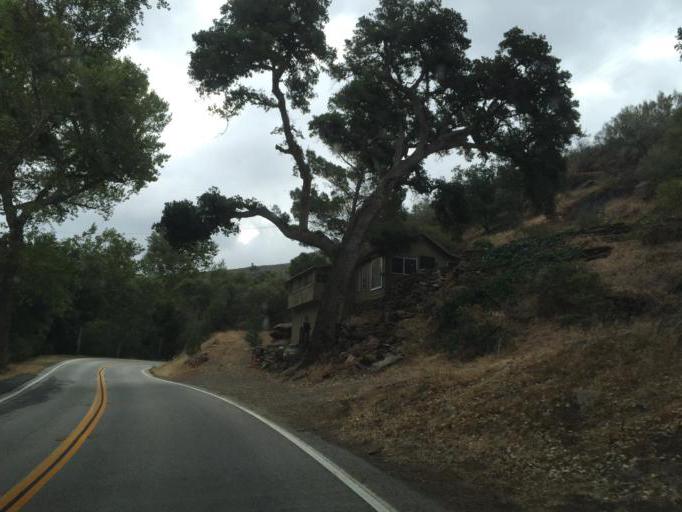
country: US
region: California
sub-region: Los Angeles County
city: Green Valley
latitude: 34.5494
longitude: -118.4300
